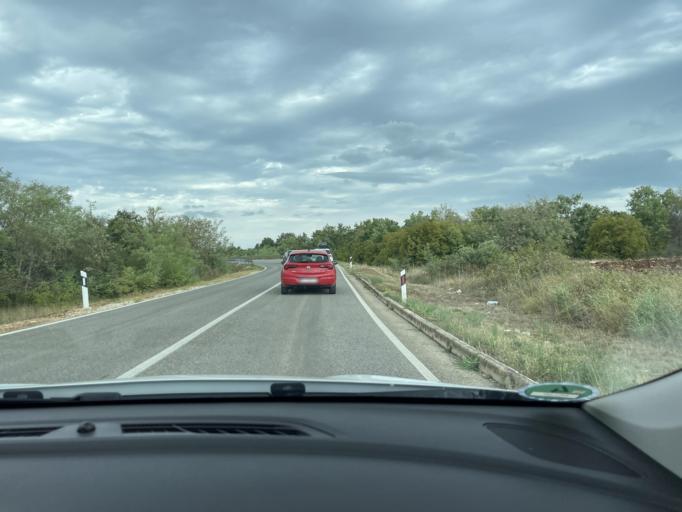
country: HR
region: Istarska
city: Vrsar
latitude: 45.1809
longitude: 13.7347
